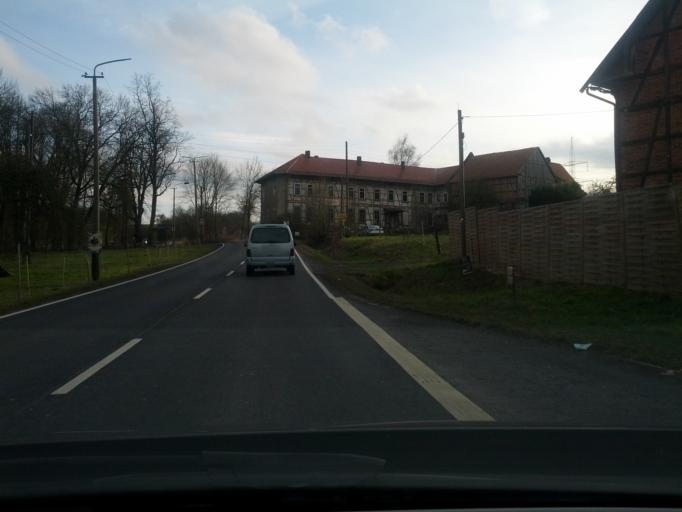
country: DE
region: Thuringia
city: Krauthausen
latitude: 51.0267
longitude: 10.2586
